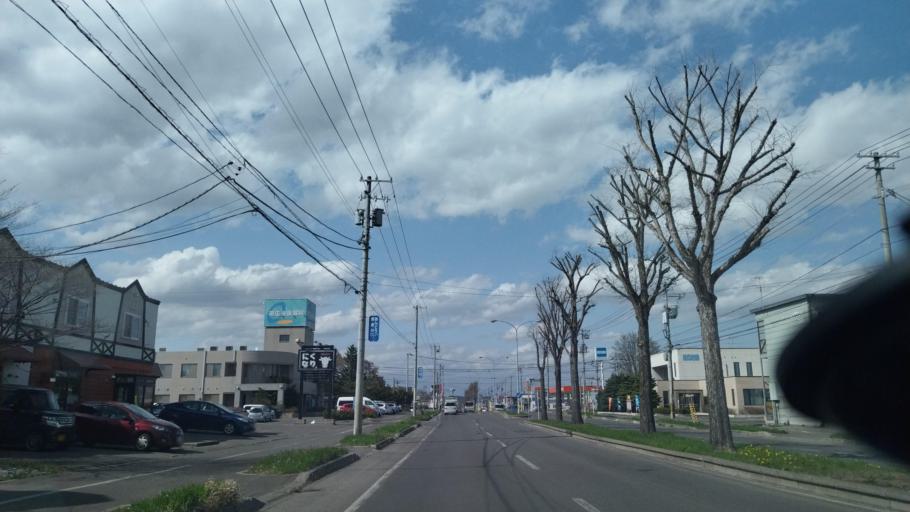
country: JP
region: Hokkaido
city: Obihiro
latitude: 42.9064
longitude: 143.1459
